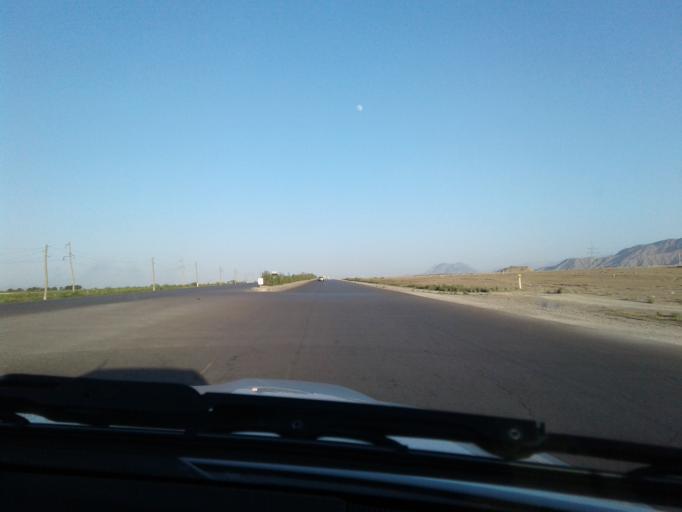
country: TM
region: Ahal
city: Baharly
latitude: 38.2366
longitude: 57.7746
